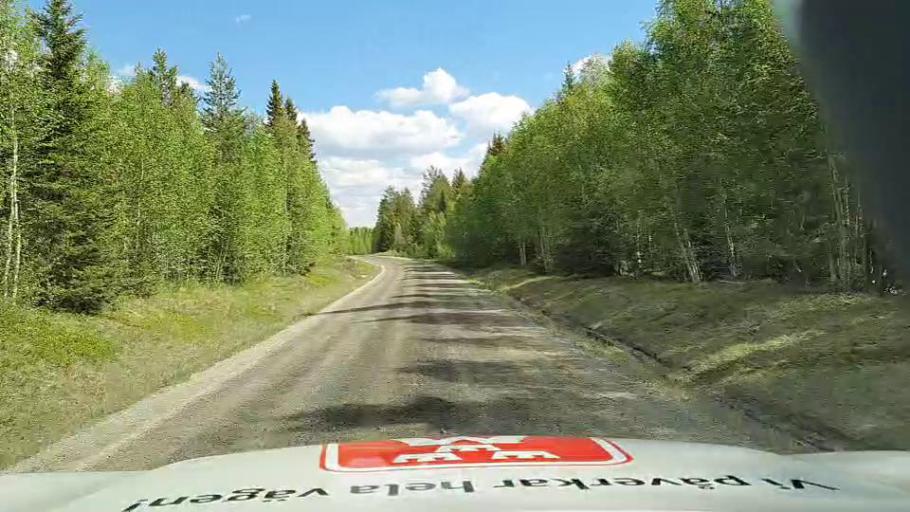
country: SE
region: Jaemtland
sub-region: Krokoms Kommun
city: Valla
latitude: 63.9648
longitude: 14.0976
